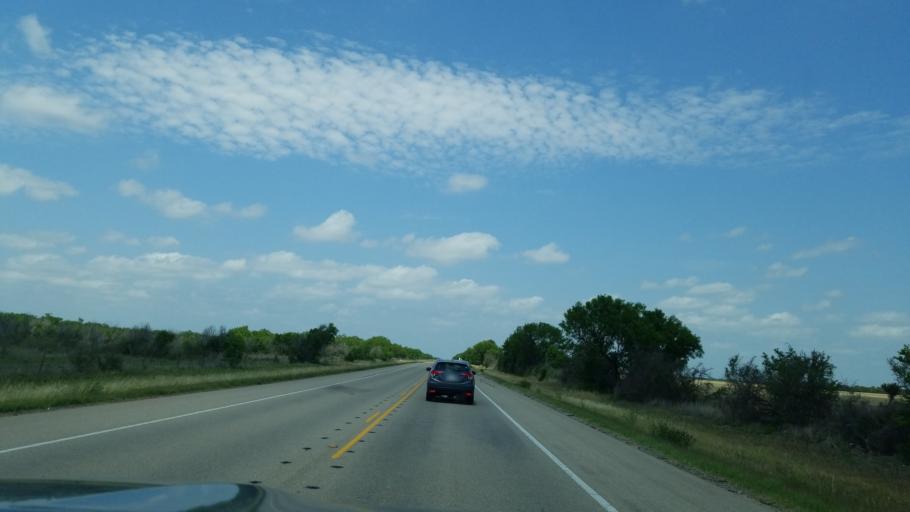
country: US
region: Texas
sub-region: Frio County
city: Pearsall
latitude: 29.0067
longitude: -99.1561
